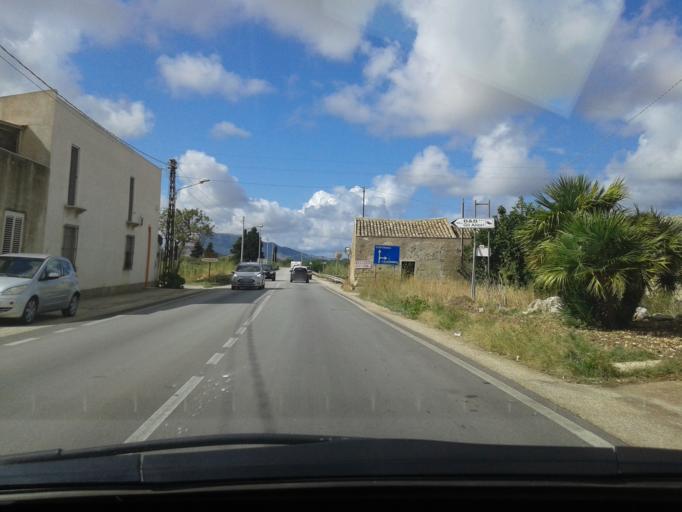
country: IT
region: Sicily
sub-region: Trapani
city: Custonaci
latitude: 38.0795
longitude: 12.7031
